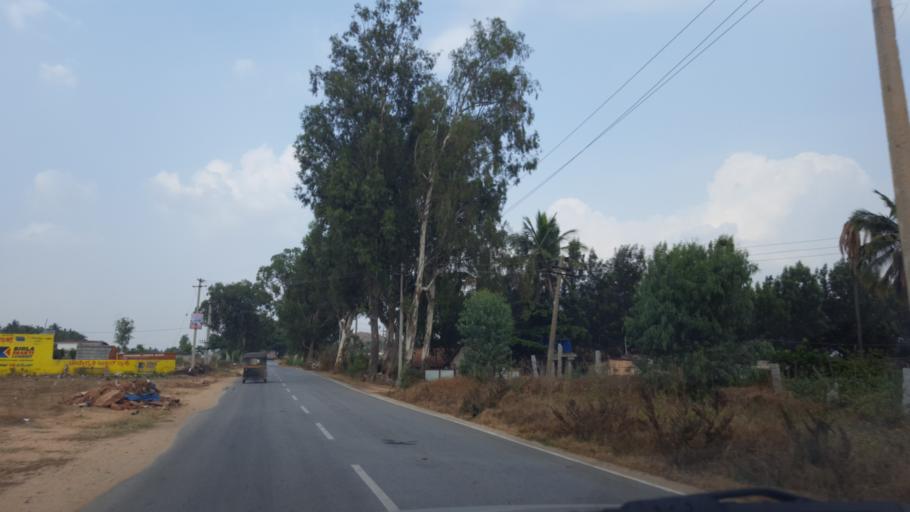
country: IN
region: Karnataka
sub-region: Chikkaballapur
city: Chik Ballapur
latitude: 13.3526
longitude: 77.6891
